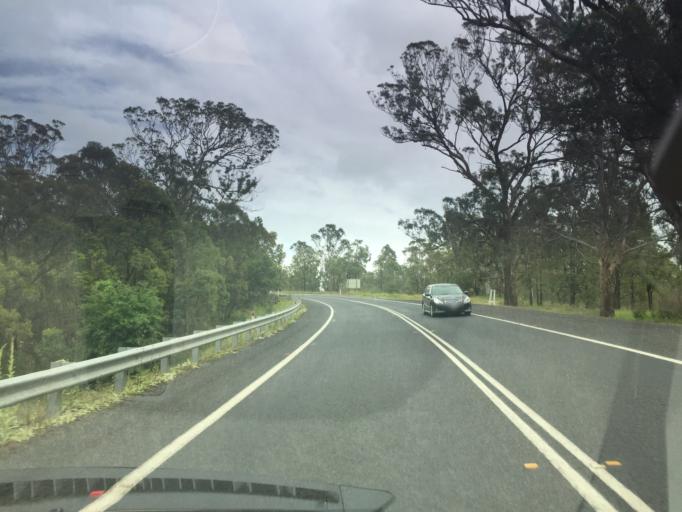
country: AU
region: New South Wales
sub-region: Bega Valley
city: Bega
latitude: -36.6342
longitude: 149.5771
